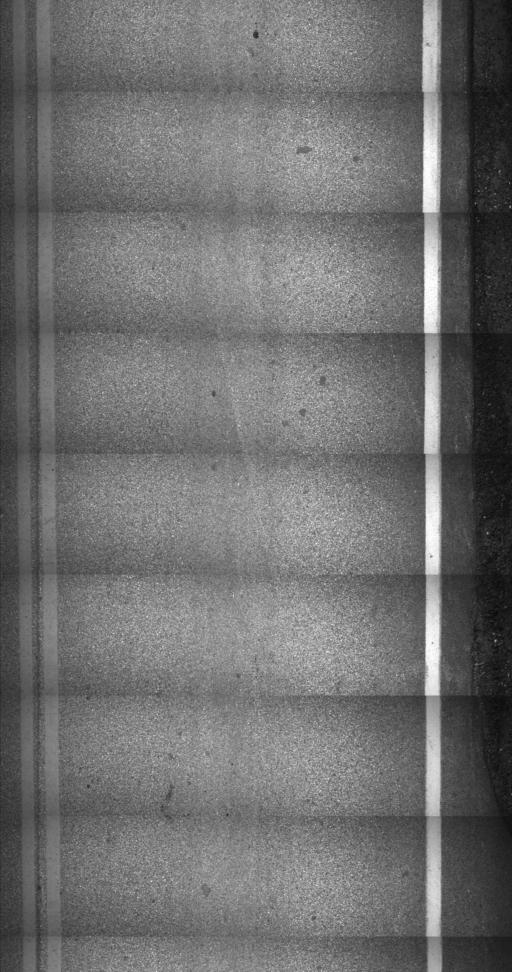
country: US
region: Vermont
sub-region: Rutland County
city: Poultney
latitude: 43.5068
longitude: -73.2351
